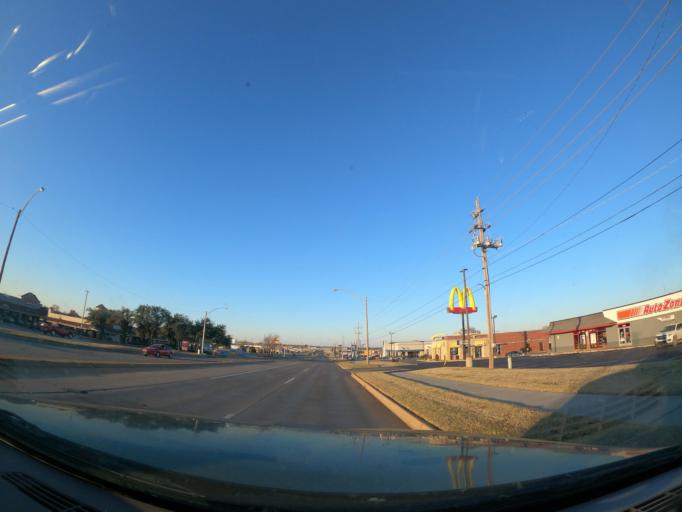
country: US
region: Oklahoma
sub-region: Tulsa County
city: Broken Arrow
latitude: 36.0910
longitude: -95.8865
